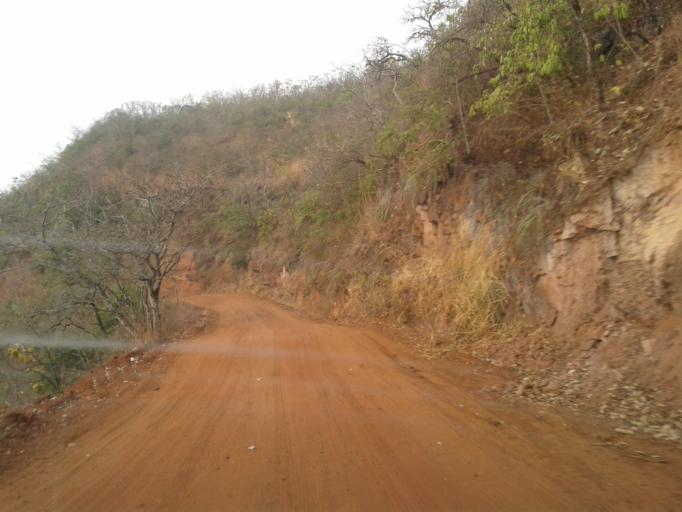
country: BR
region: Minas Gerais
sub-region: Santa Vitoria
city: Santa Vitoria
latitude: -19.1833
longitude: -49.8588
